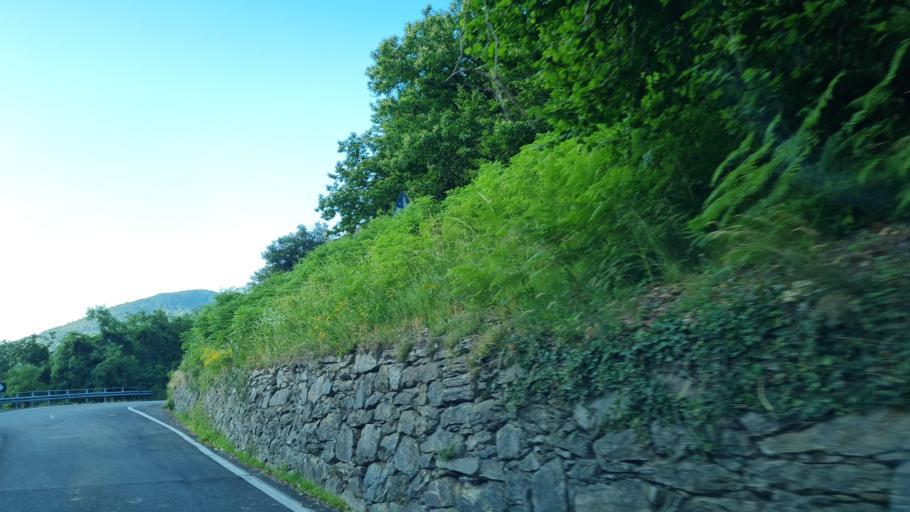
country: IT
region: Piedmont
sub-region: Provincia di Torino
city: Pont-Canavese
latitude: 45.4296
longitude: 7.5888
